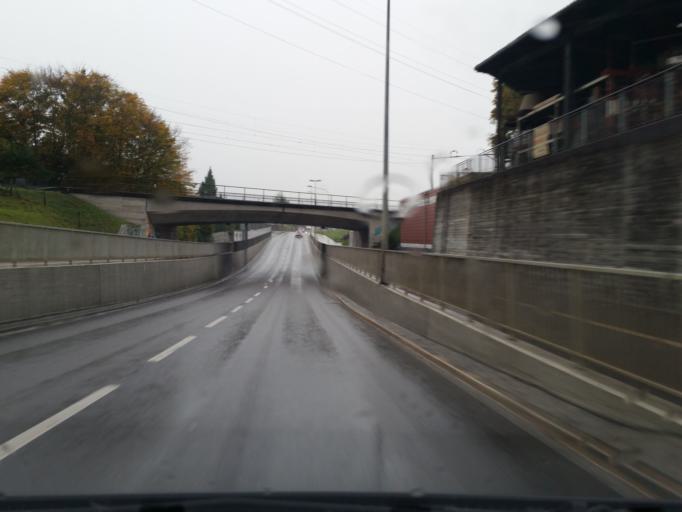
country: CH
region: Thurgau
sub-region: Weinfelden District
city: Weinfelden
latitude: 47.5620
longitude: 9.1187
